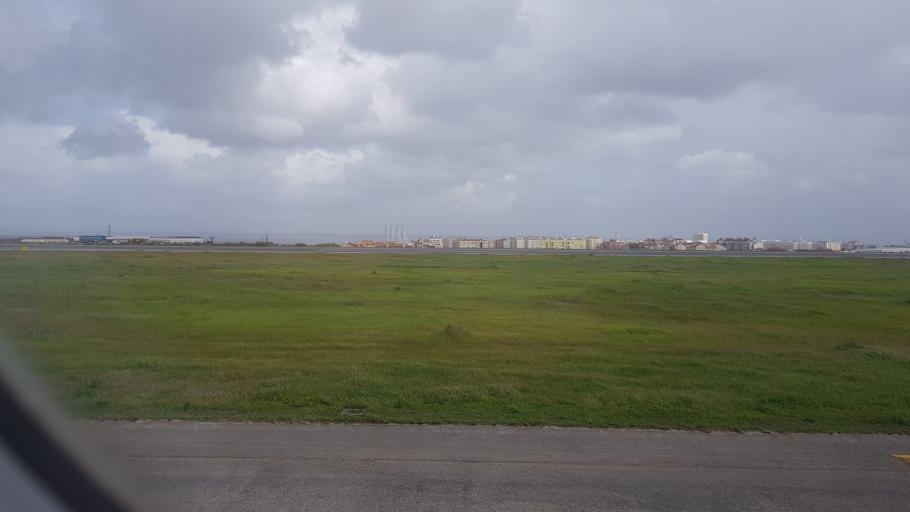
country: PT
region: Lisbon
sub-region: Loures
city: Camarate
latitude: 38.7960
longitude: -9.1306
